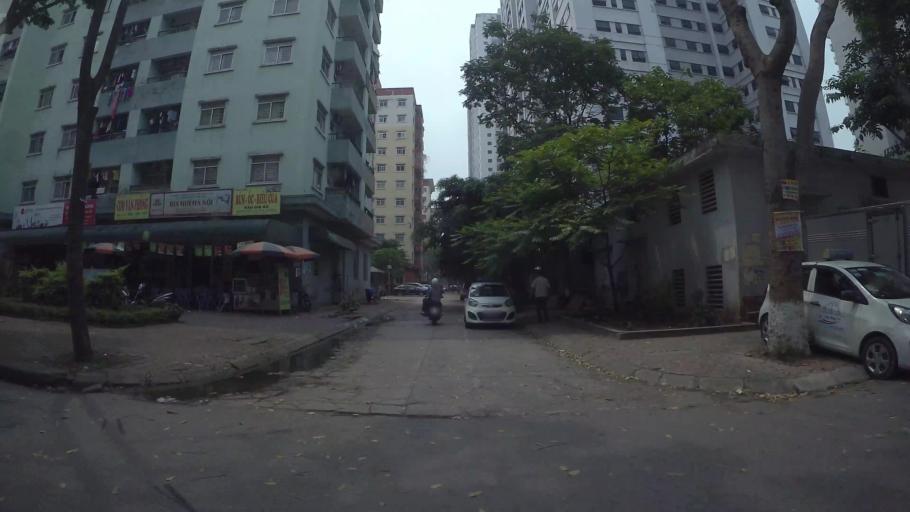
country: VN
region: Ha Noi
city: Van Dien
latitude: 20.9649
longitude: 105.8316
